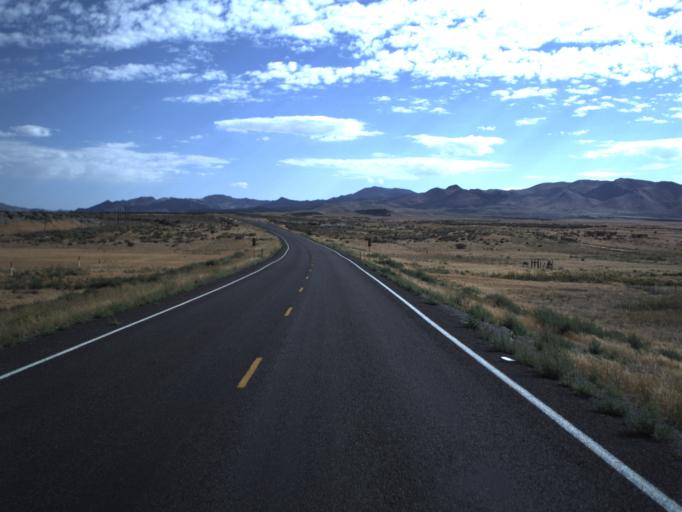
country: US
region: Utah
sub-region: Juab County
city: Mona
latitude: 39.7092
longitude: -112.2073
